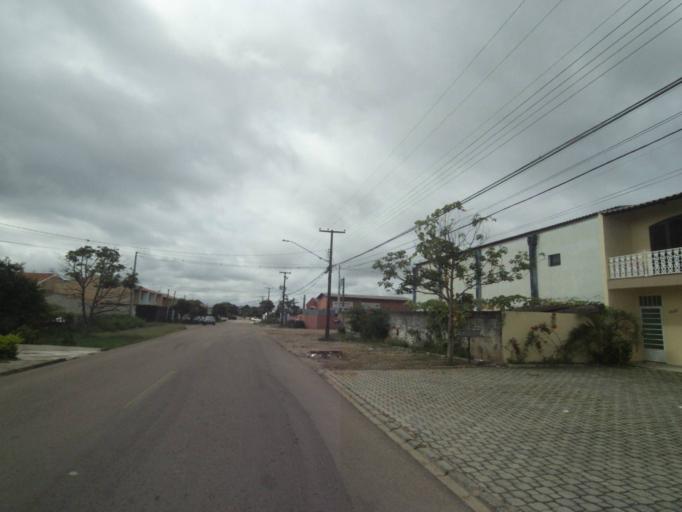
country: BR
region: Parana
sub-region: Pinhais
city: Pinhais
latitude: -25.4619
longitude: -49.2176
